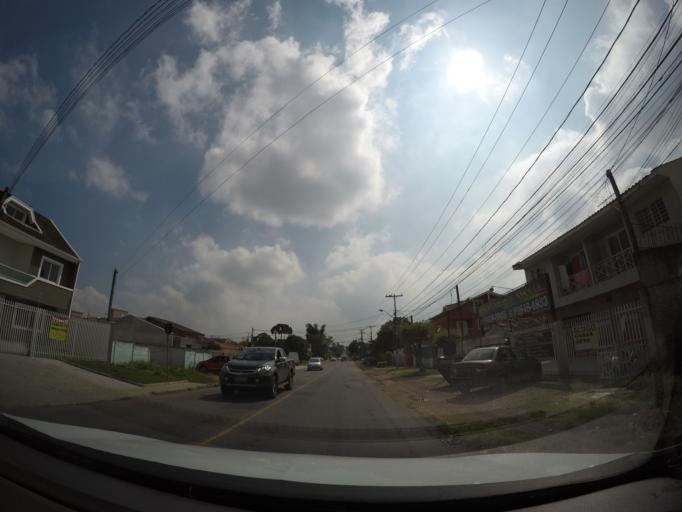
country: BR
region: Parana
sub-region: Sao Jose Dos Pinhais
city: Sao Jose dos Pinhais
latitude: -25.4940
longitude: -49.2537
